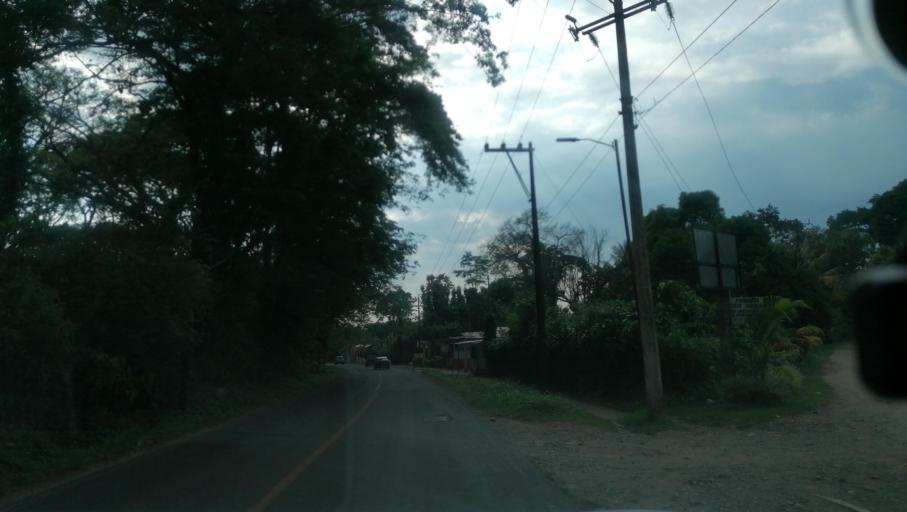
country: MX
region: Chiapas
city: Cacahoatan
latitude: 15.0027
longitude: -92.1595
